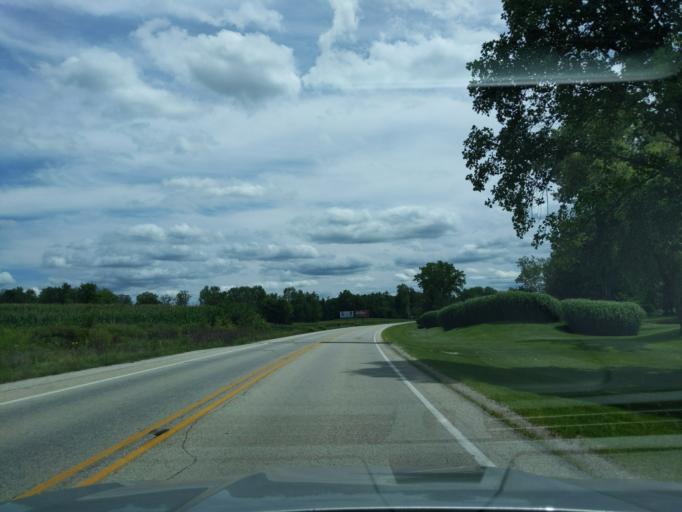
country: US
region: Indiana
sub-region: Ripley County
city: Batesville
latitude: 39.3100
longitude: -85.2272
